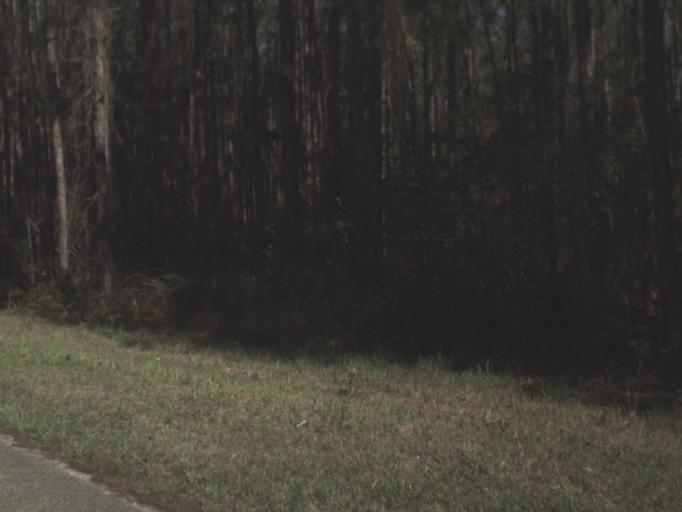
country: US
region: Florida
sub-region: Gulf County
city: Port Saint Joe
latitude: 29.8571
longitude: -85.2491
